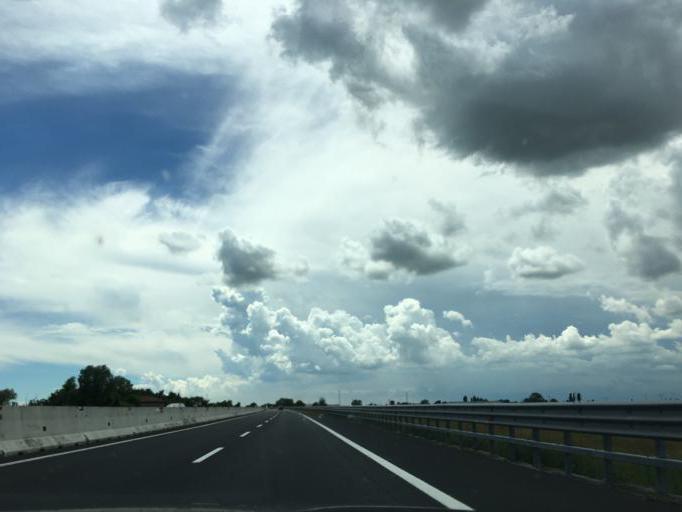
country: IT
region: Veneto
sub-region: Provincia di Venezia
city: Summaga
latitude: 45.7858
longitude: 12.7917
